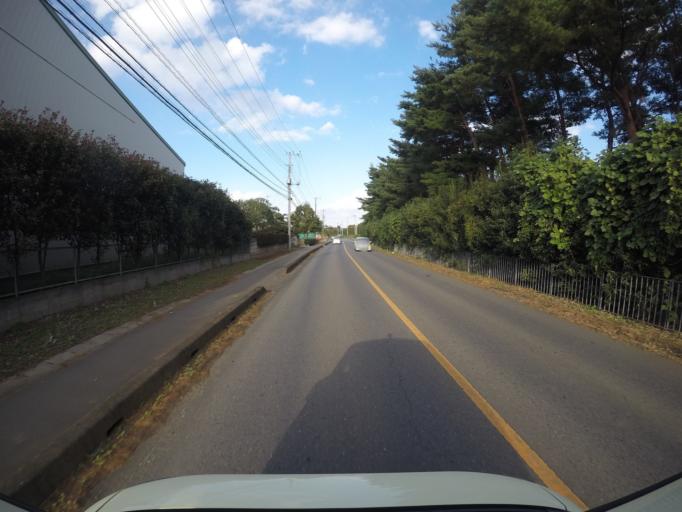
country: JP
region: Ibaraki
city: Naka
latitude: 36.0551
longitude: 140.0864
